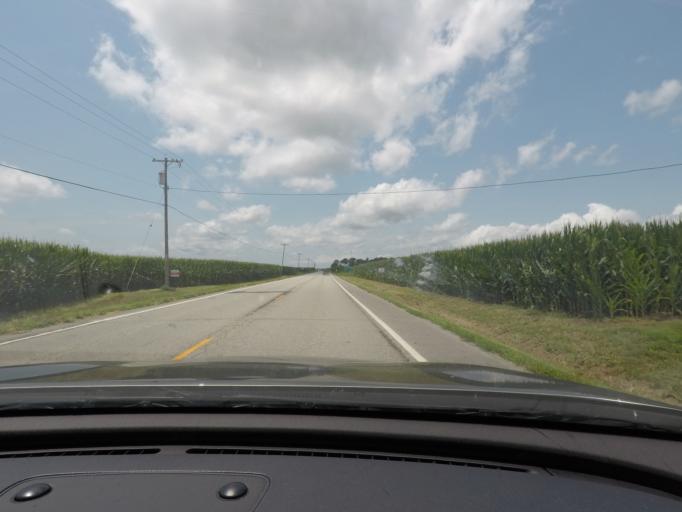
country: US
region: Missouri
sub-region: Saline County
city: Marshall
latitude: 39.1938
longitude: -93.3699
